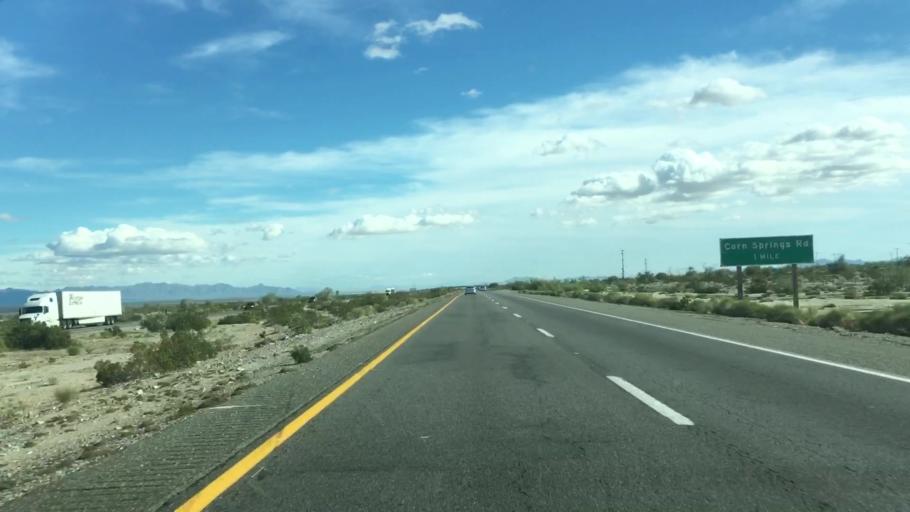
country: US
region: California
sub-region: Imperial County
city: Niland
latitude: 33.6877
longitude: -115.2614
